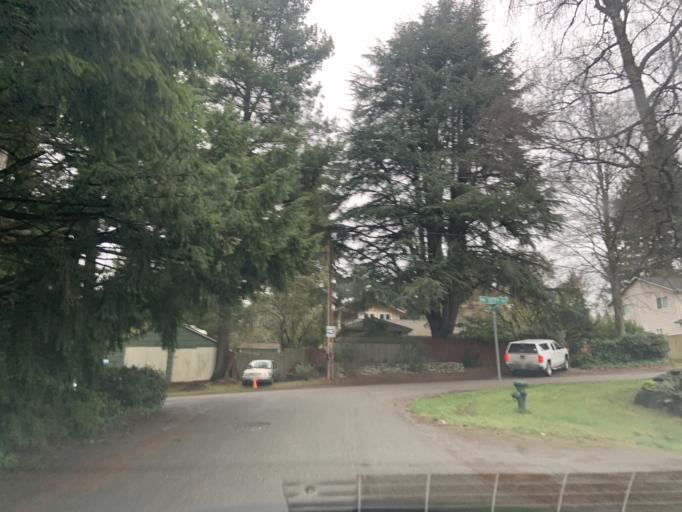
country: US
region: Washington
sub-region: King County
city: Lake Forest Park
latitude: 47.7135
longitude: -122.2866
